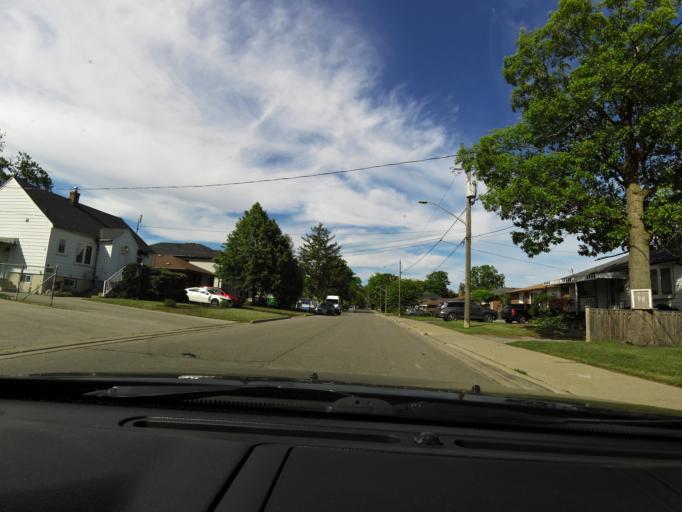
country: CA
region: Ontario
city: Mississauga
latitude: 43.5614
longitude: -79.5851
